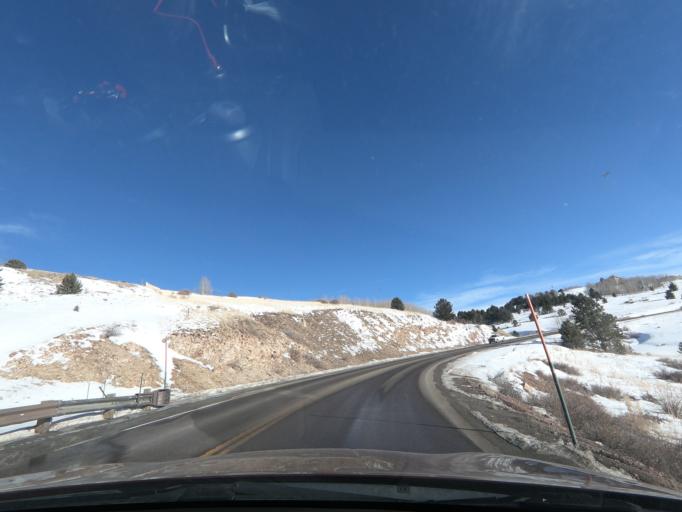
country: US
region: Colorado
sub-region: Teller County
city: Cripple Creek
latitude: 38.7550
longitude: -105.1654
